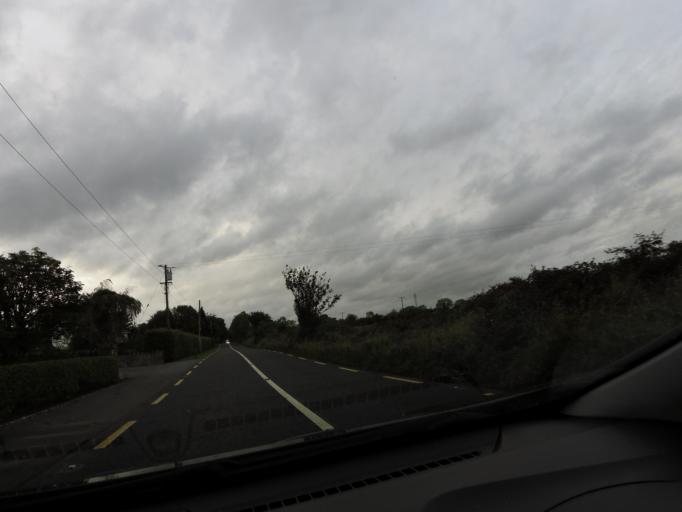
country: IE
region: Leinster
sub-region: An Iarmhi
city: Athlone
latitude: 53.3915
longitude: -7.8699
